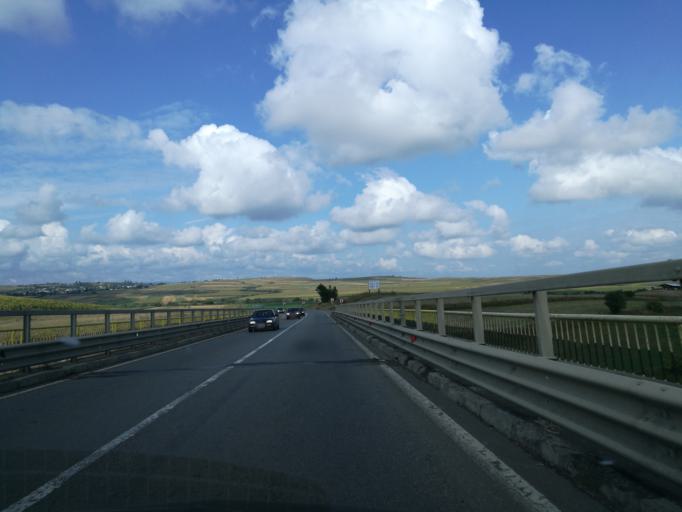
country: RO
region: Suceava
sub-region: Comuna Stroesti
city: Stroesti
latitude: 47.6230
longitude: 26.0914
